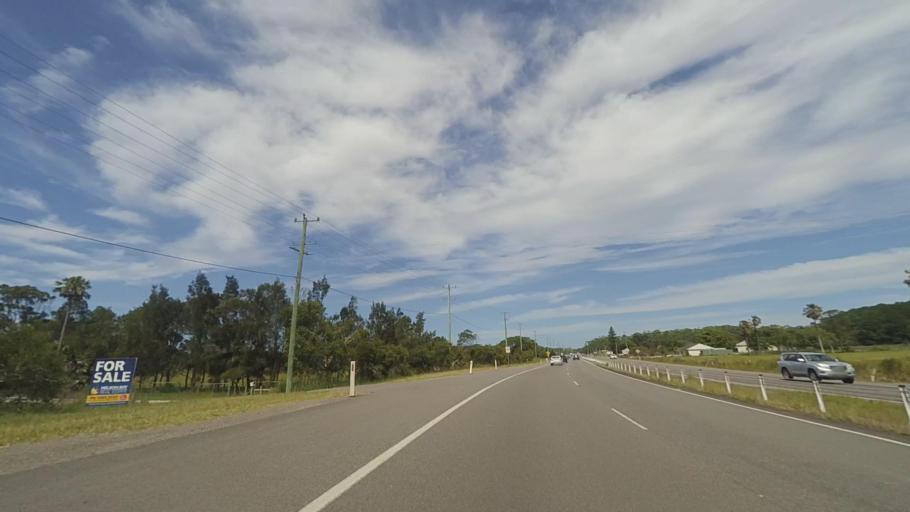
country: AU
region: New South Wales
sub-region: Port Stephens Shire
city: Anna Bay
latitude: -32.7663
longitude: 152.0149
